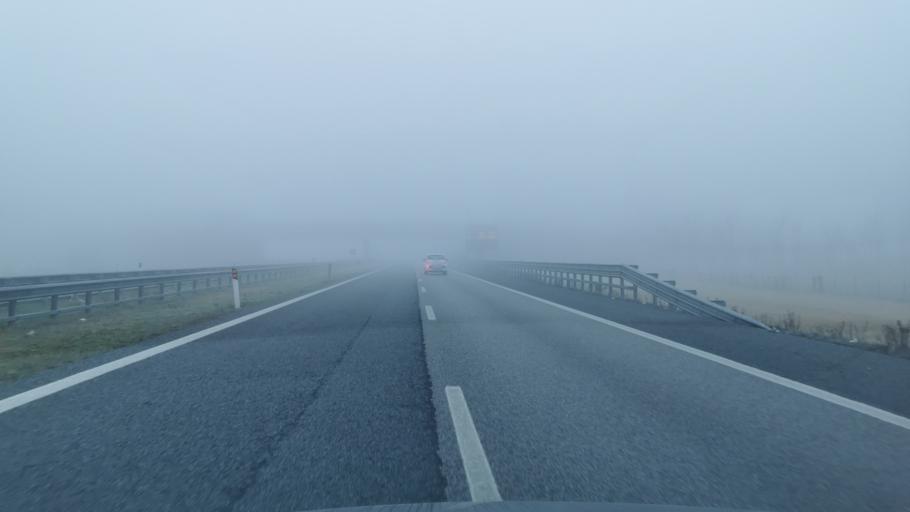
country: IT
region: Piedmont
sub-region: Provincia di Torino
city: Villastellone
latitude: 44.9335
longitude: 7.7240
